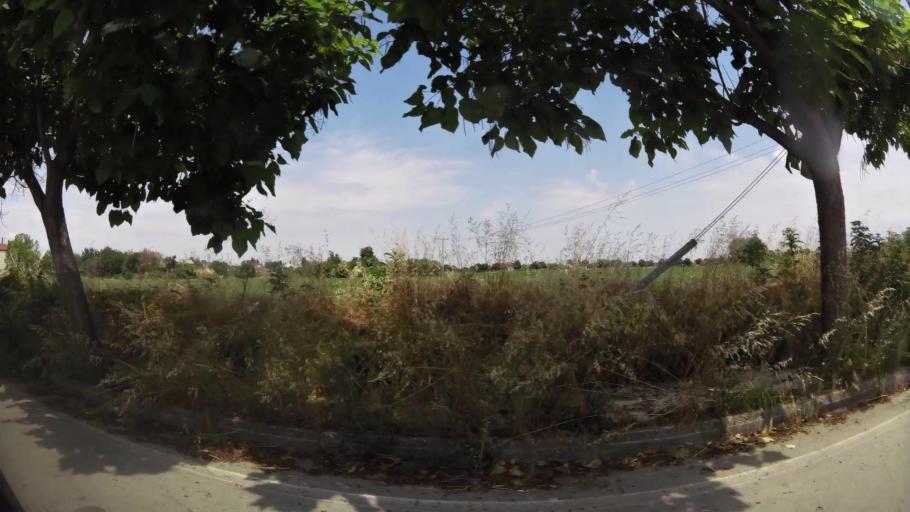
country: GR
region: Central Macedonia
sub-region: Nomos Pierias
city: Peristasi
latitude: 40.2649
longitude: 22.5351
